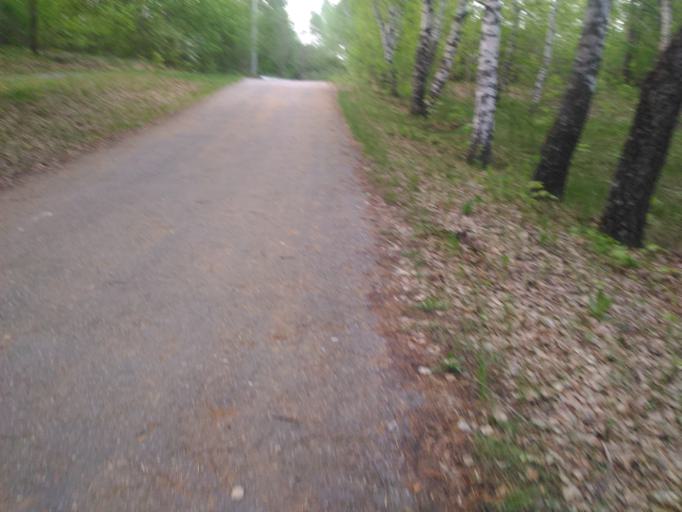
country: RU
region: Ulyanovsk
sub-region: Ulyanovskiy Rayon
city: Ulyanovsk
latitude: 54.2728
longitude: 48.3554
